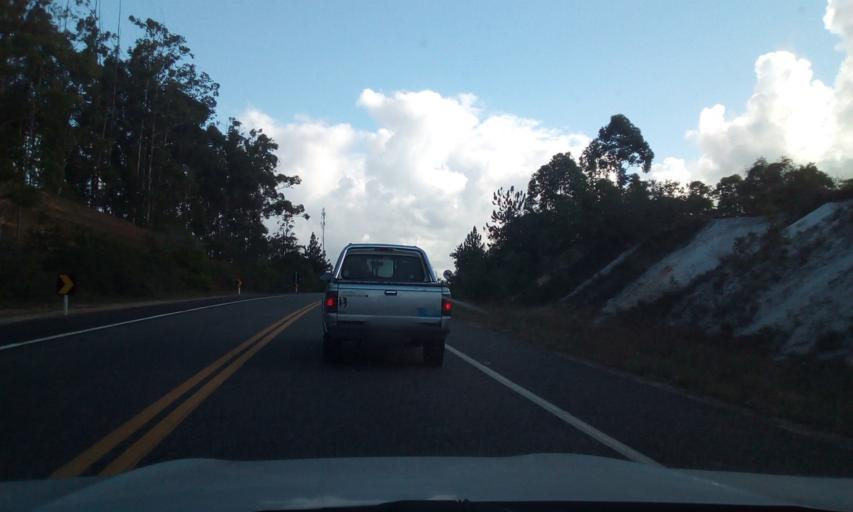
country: BR
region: Bahia
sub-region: Entre Rios
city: Entre Rios
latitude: -12.3065
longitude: -37.9037
